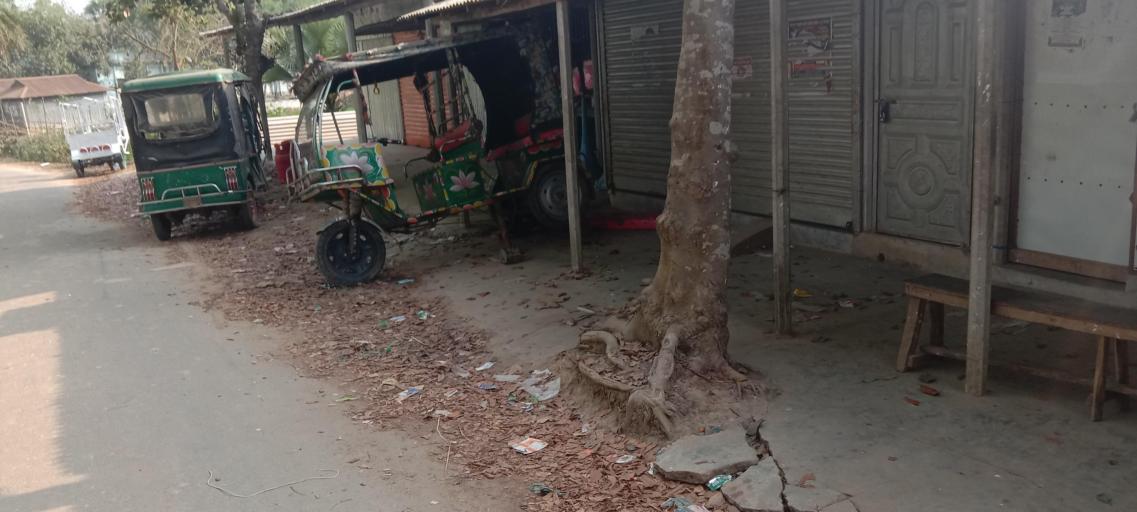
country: BD
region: Dhaka
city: Sakhipur
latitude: 24.4619
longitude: 90.3145
